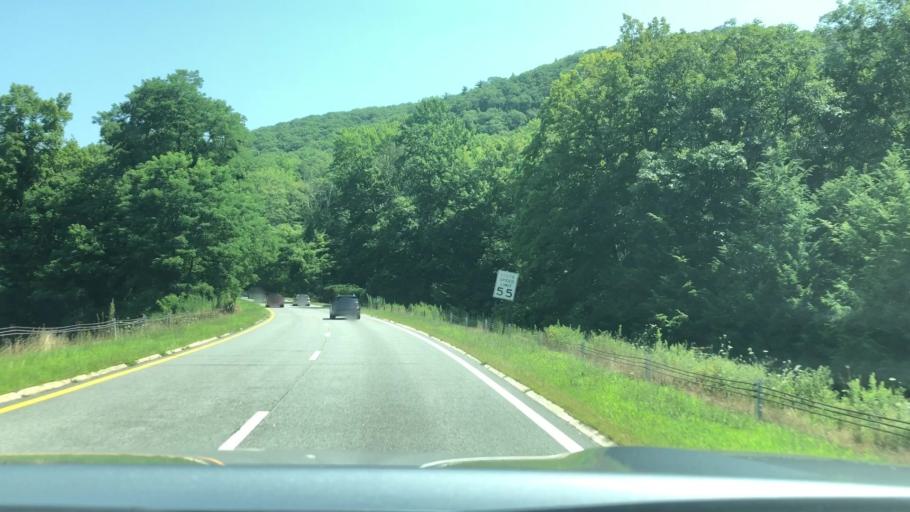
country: US
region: New York
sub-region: Orange County
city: Fort Montgomery
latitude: 41.3126
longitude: -74.0189
